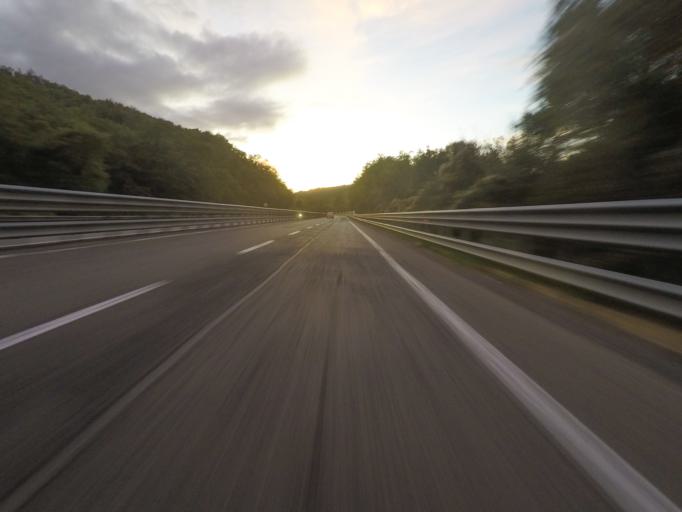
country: IT
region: Tuscany
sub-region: Province of Arezzo
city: Lucignano
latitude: 43.2562
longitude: 11.6944
